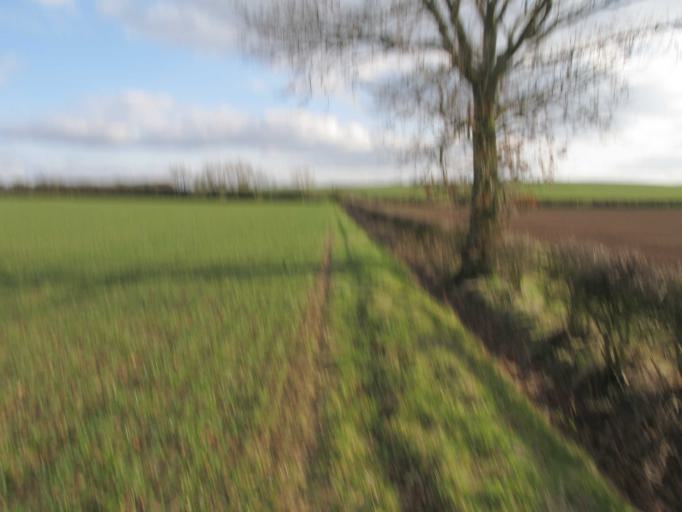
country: GB
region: England
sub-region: Nottinghamshire
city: Misterton
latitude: 53.3873
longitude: -0.8700
